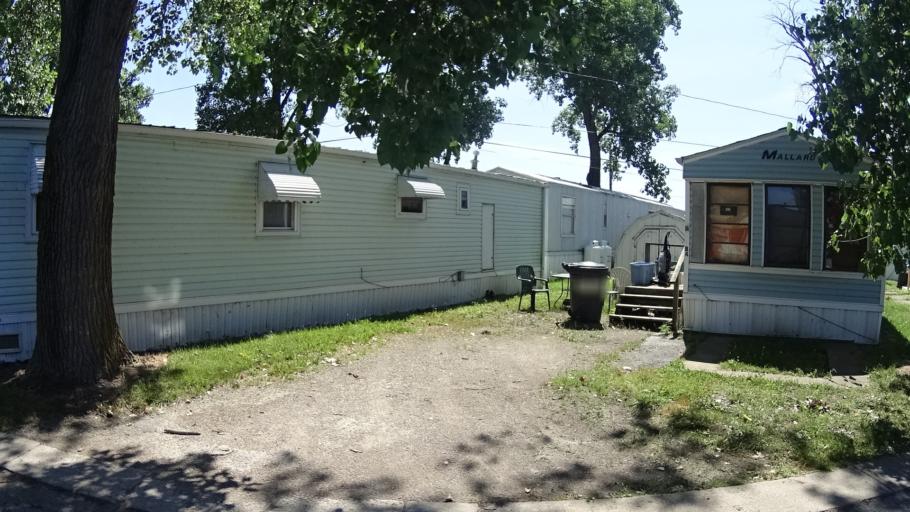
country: US
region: Ohio
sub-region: Ottawa County
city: Port Clinton
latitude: 41.4320
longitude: -82.8938
